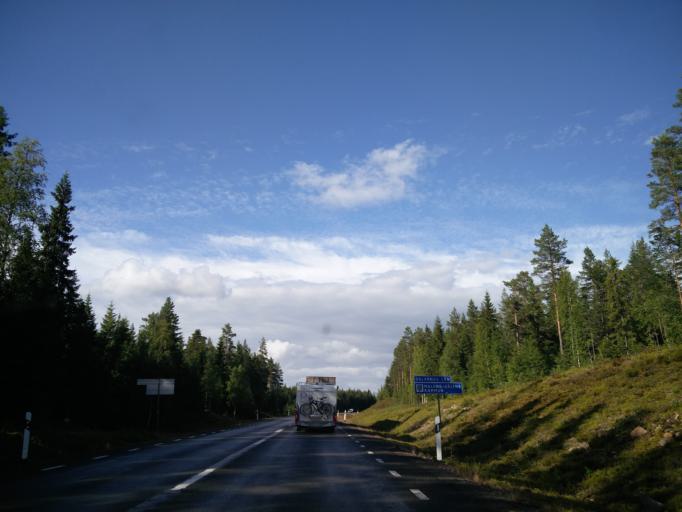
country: SE
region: Dalarna
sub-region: Malung-Saelens kommun
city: Malung
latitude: 60.5095
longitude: 13.4333
